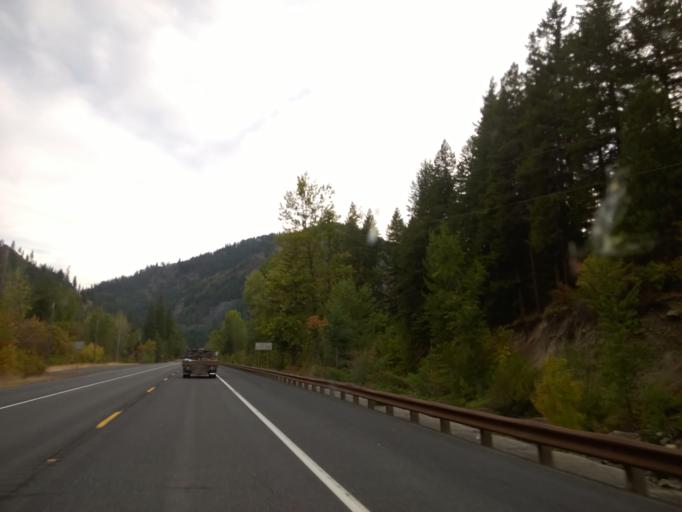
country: US
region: Washington
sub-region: Chelan County
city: Leavenworth
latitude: 47.4722
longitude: -120.6566
